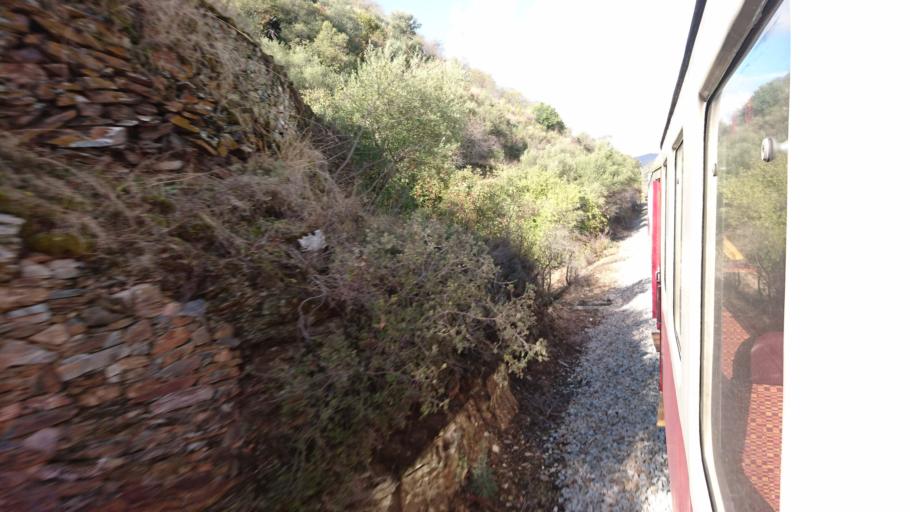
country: PT
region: Guarda
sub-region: Vila Nova de Foz Coa
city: Vila Nova de Foz Coa
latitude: 41.1334
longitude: -7.2064
